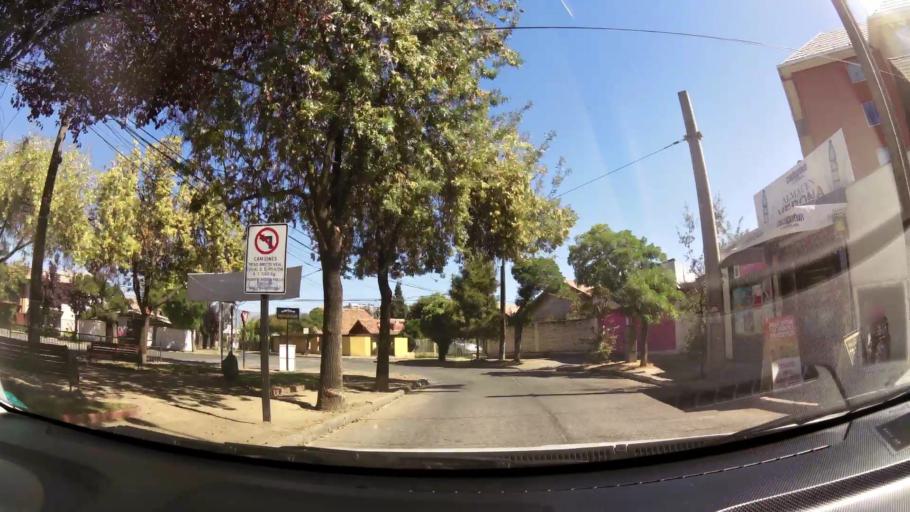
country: CL
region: O'Higgins
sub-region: Provincia de Cachapoal
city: Rancagua
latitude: -34.1742
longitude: -70.7305
